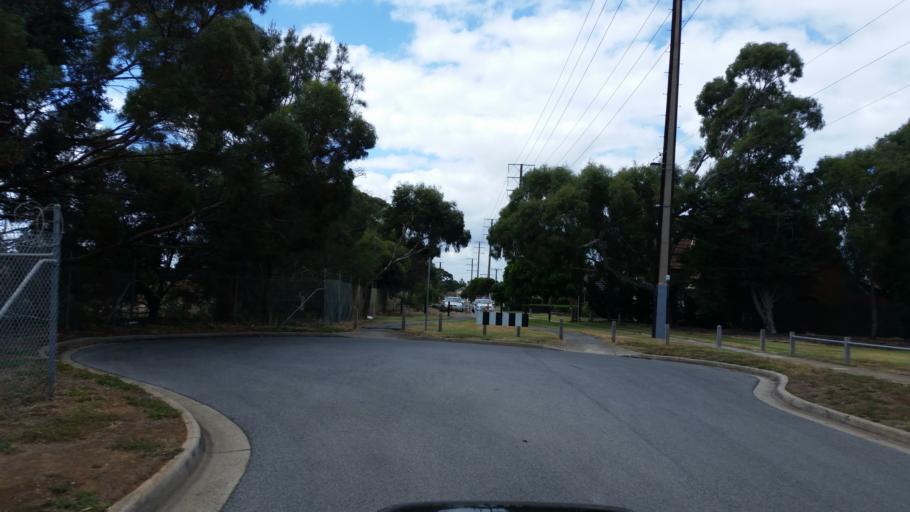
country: AU
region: South Australia
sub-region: Charles Sturt
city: Seaton
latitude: -34.9002
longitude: 138.5109
